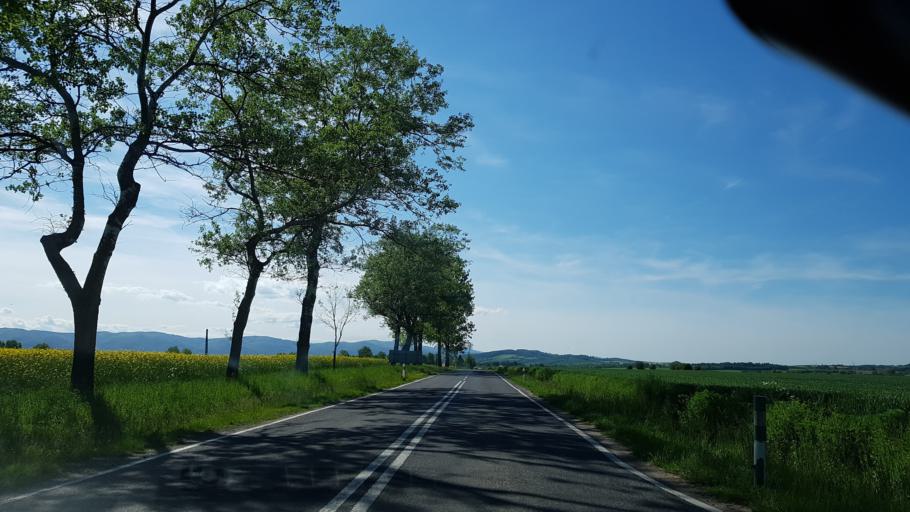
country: PL
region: Lower Silesian Voivodeship
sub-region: Powiat zabkowicki
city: Zabkowice Slaskie
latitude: 50.5936
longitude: 16.7863
